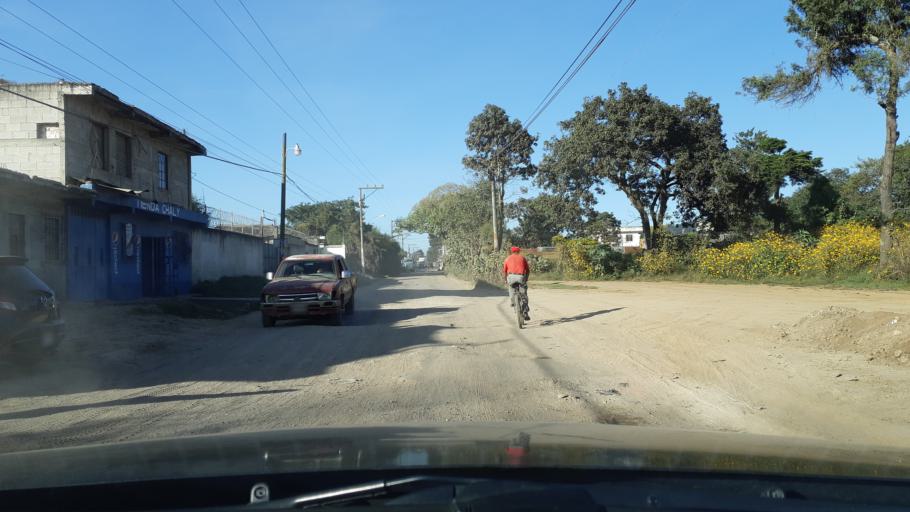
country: GT
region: Chimaltenango
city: El Tejar
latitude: 14.6446
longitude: -90.7988
